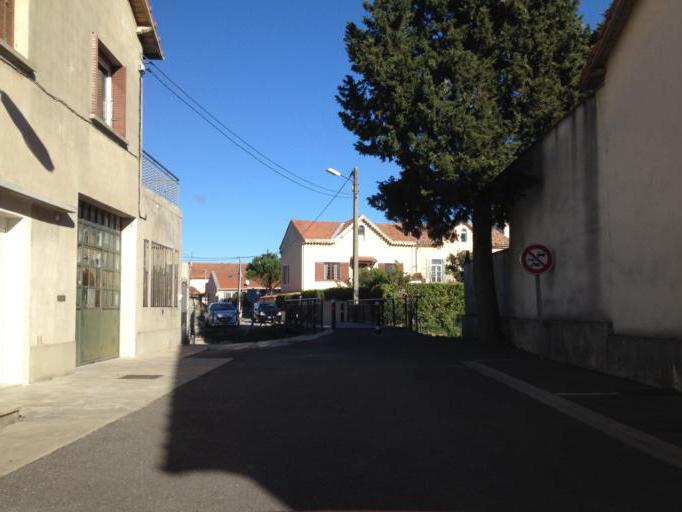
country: FR
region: Provence-Alpes-Cote d'Azur
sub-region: Departement du Vaucluse
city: Orange
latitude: 44.1327
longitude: 4.8149
